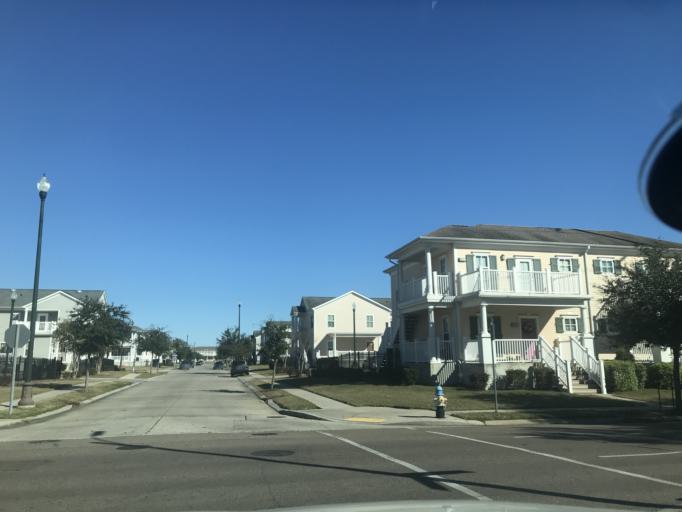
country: US
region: Louisiana
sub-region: Orleans Parish
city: New Orleans
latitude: 29.9506
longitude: -90.0959
